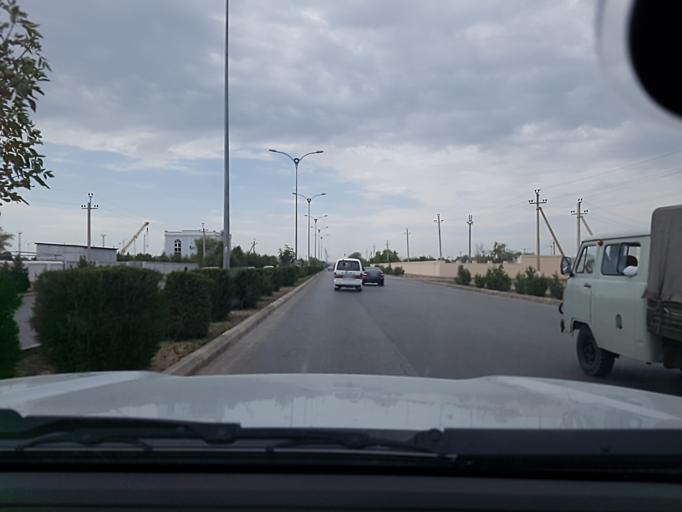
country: TM
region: Dasoguz
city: Dasoguz
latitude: 41.8580
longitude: 59.9429
